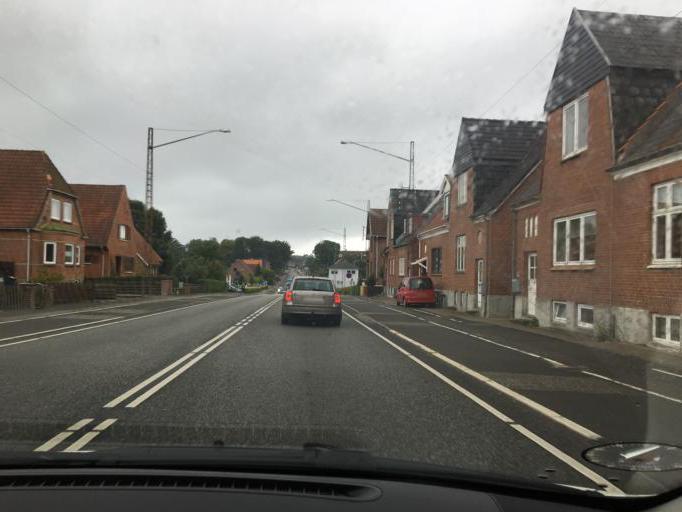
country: DK
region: South Denmark
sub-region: Middelfart Kommune
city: Middelfart
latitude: 55.5004
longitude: 9.7362
